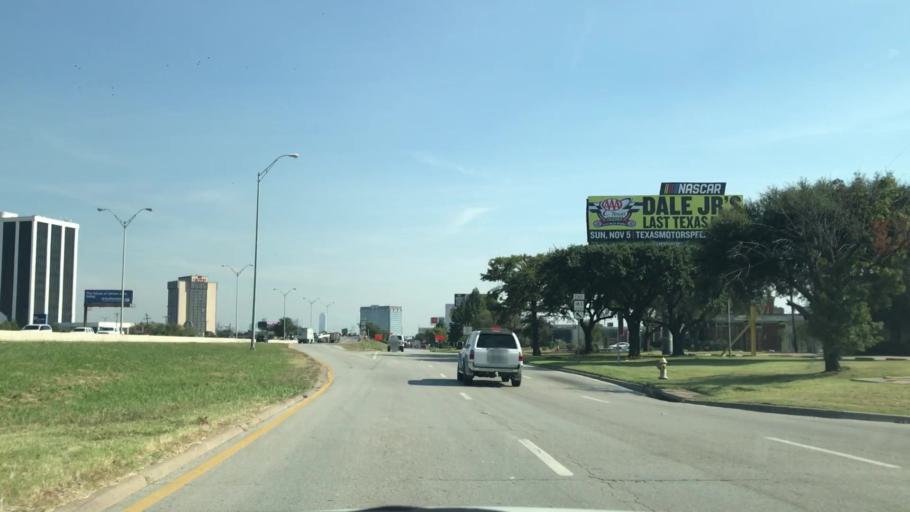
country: US
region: Texas
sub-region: Dallas County
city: Irving
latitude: 32.8199
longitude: -96.8750
